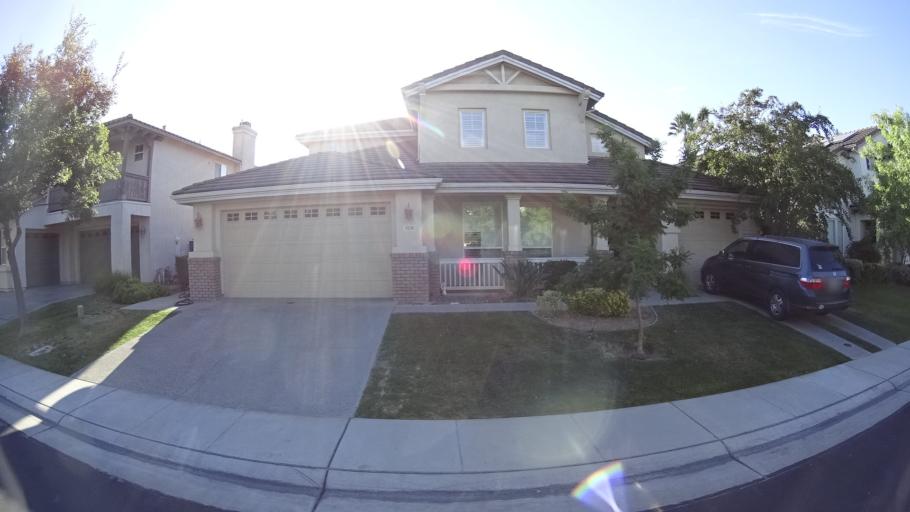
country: US
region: California
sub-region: Sacramento County
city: Laguna
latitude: 38.3998
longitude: -121.4685
